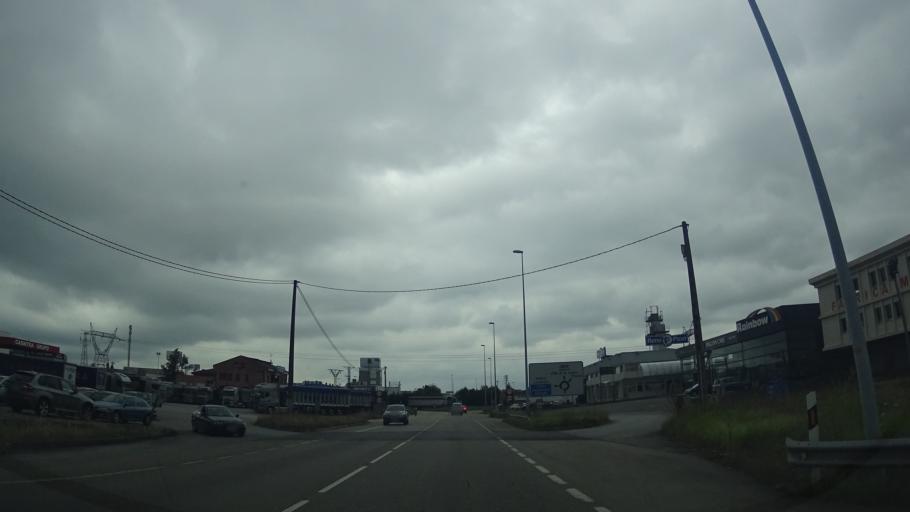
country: ES
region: Asturias
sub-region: Province of Asturias
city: Norena
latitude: 43.3833
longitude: -5.7597
